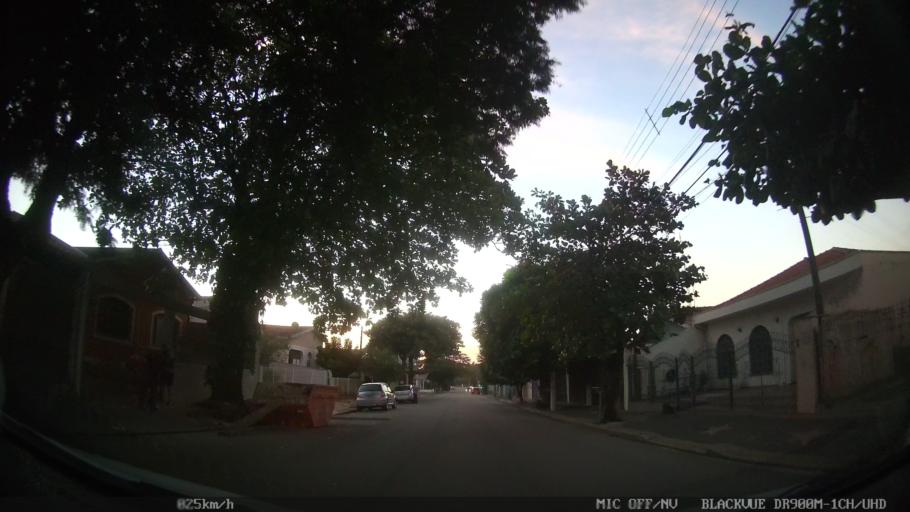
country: BR
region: Sao Paulo
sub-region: Sumare
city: Sumare
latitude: -22.8138
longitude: -47.2745
